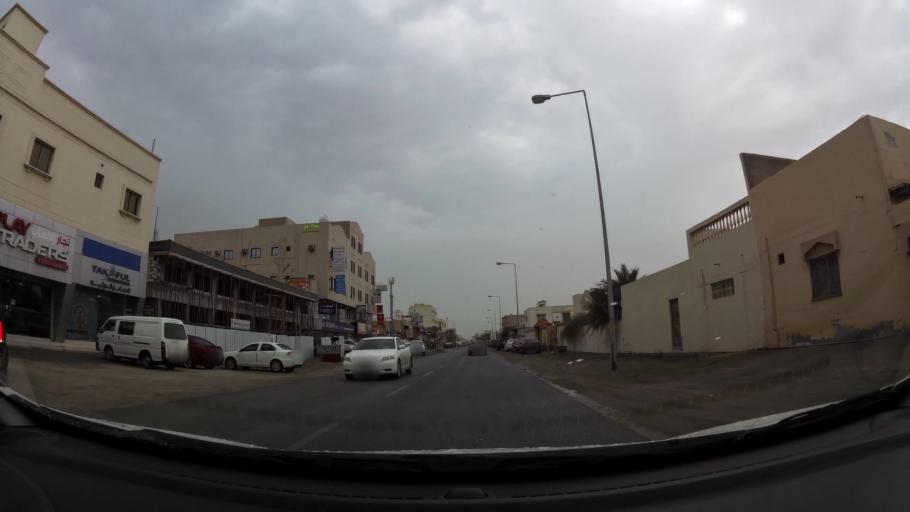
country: BH
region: Northern
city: Madinat `Isa
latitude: 26.1665
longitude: 50.5689
